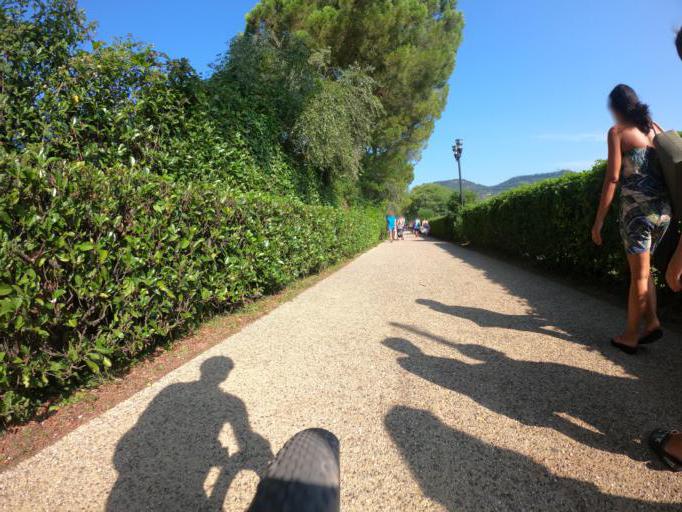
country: IT
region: Veneto
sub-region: Provincia di Verona
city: Bardolino
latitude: 45.5551
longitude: 10.7172
